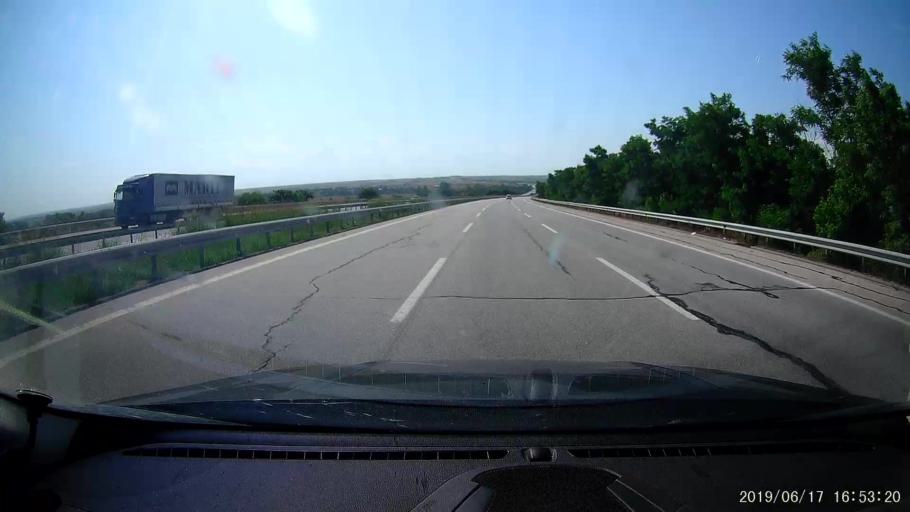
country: TR
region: Kirklareli
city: Inece
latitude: 41.5624
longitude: 27.0258
